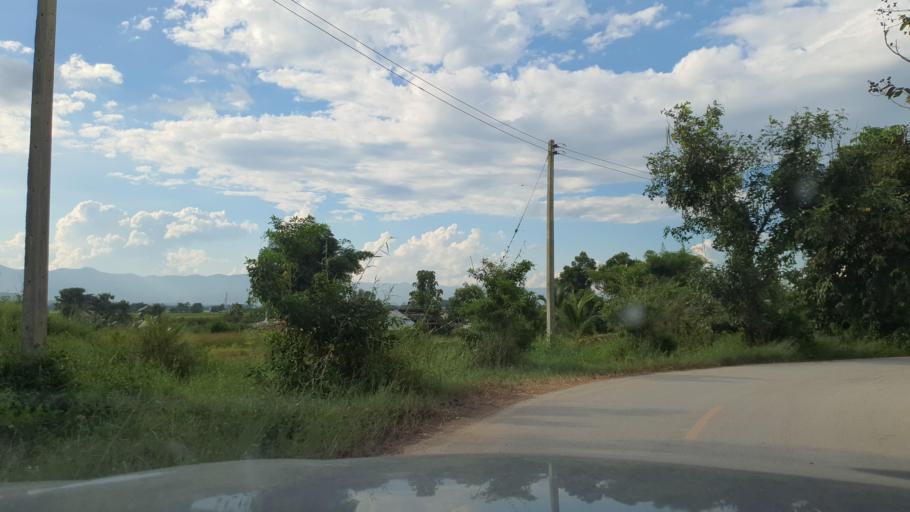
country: TH
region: Phayao
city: Phayao
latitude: 19.1876
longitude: 99.8559
